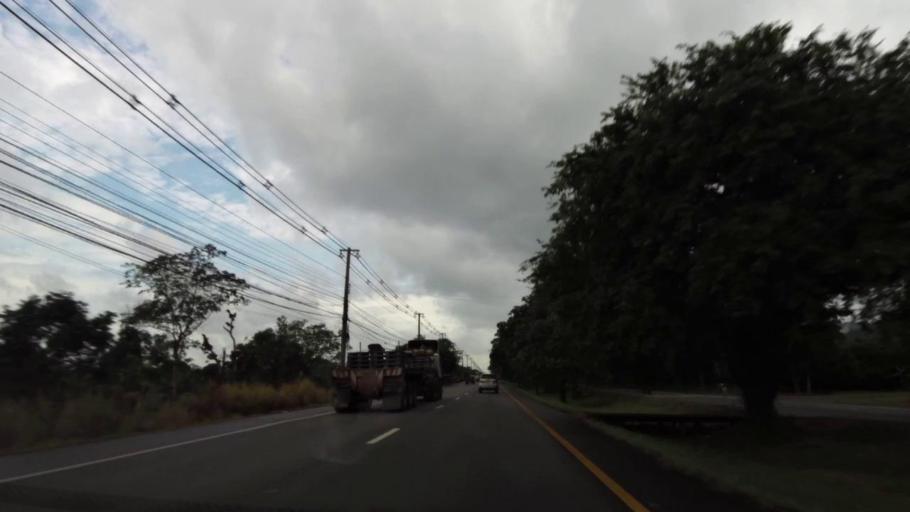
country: TH
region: Chanthaburi
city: Khlung
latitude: 12.4731
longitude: 102.1916
